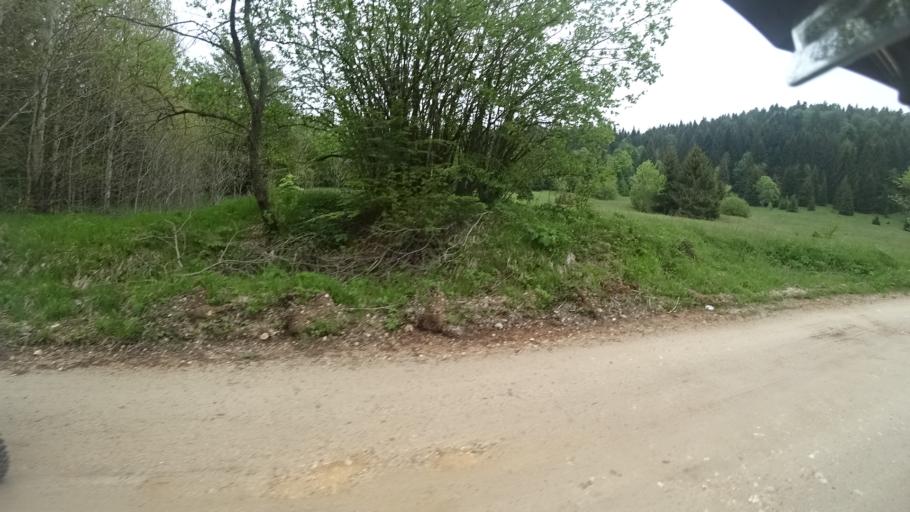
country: BA
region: Federation of Bosnia and Herzegovina
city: Bihac
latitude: 44.6471
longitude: 15.8563
